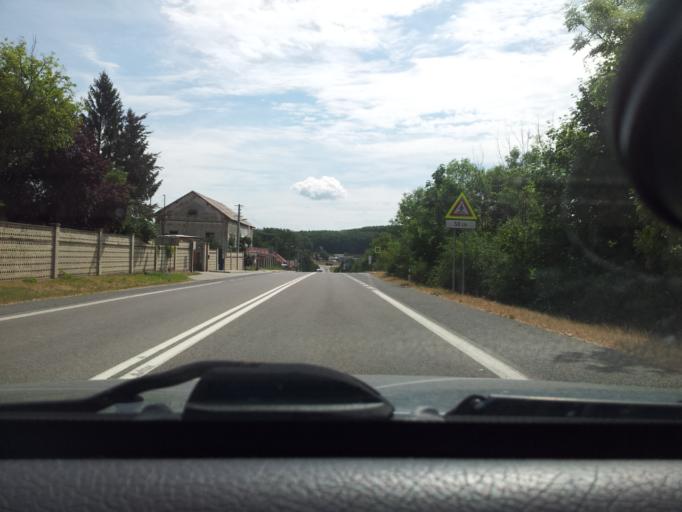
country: SK
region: Nitriansky
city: Zlate Moravce
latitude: 48.3561
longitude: 18.4718
